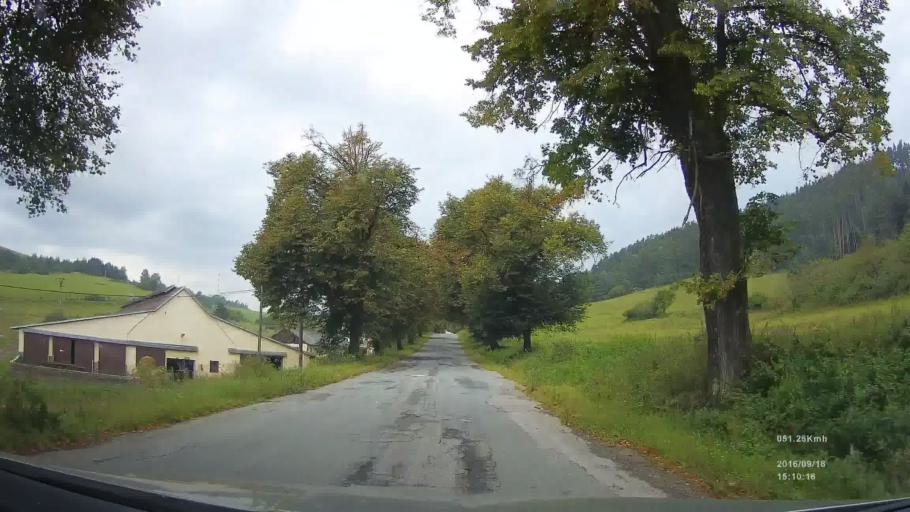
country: SK
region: Presovsky
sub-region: Okres Presov
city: Levoca
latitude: 49.0184
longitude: 20.5012
